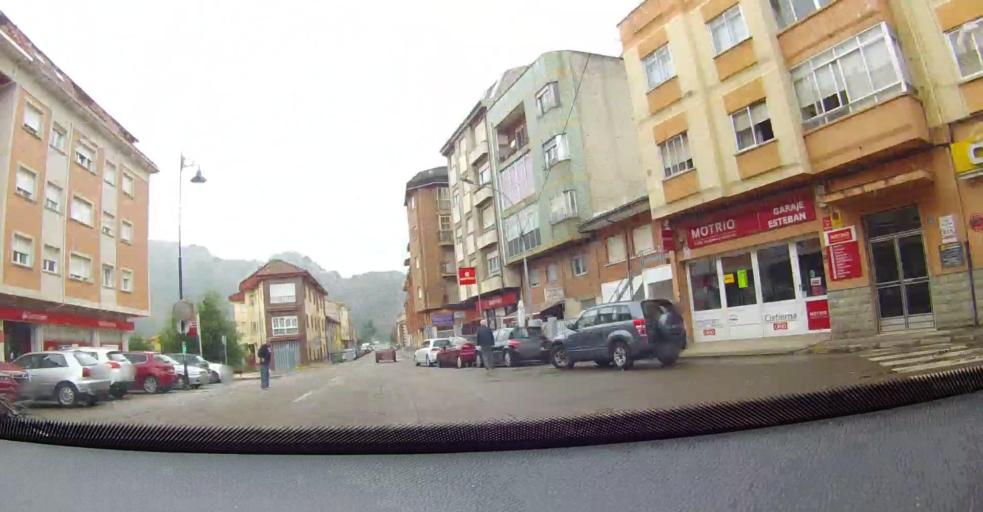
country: ES
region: Castille and Leon
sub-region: Provincia de Leon
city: Cistierna
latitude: 42.8054
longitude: -5.1292
